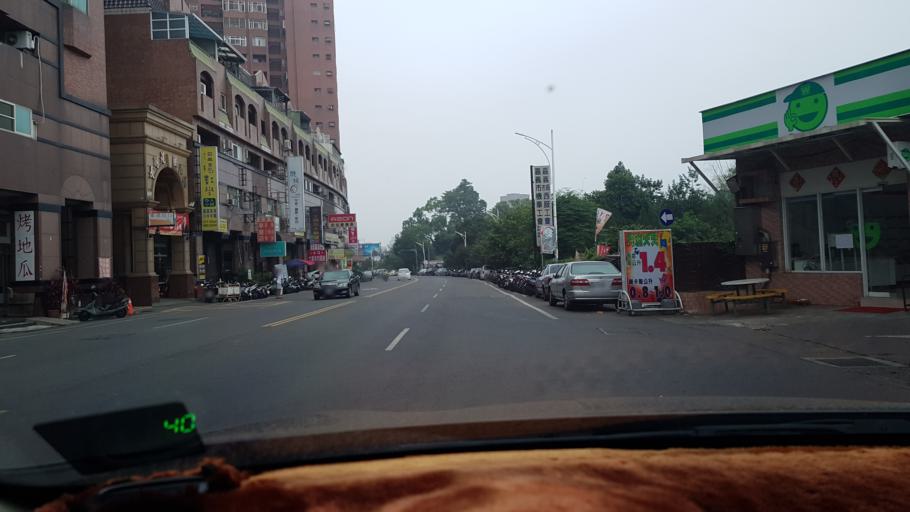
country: TW
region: Taiwan
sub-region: Chiayi
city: Jiayi Shi
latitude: 23.4906
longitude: 120.4617
